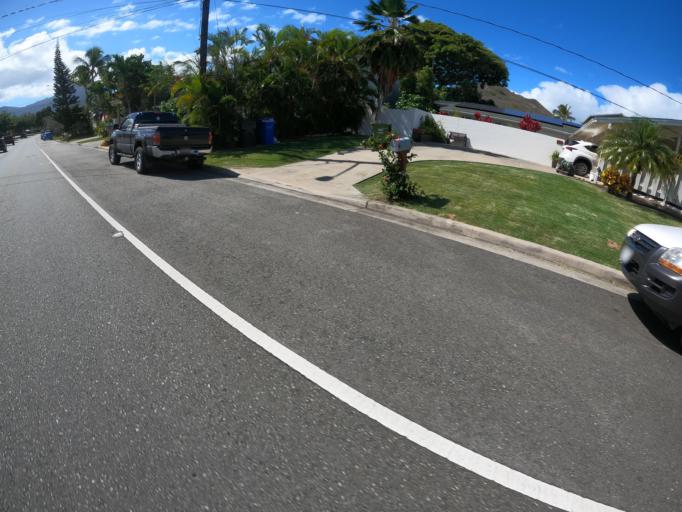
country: US
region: Hawaii
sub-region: Honolulu County
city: Kailua
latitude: 21.4146
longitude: -157.7515
